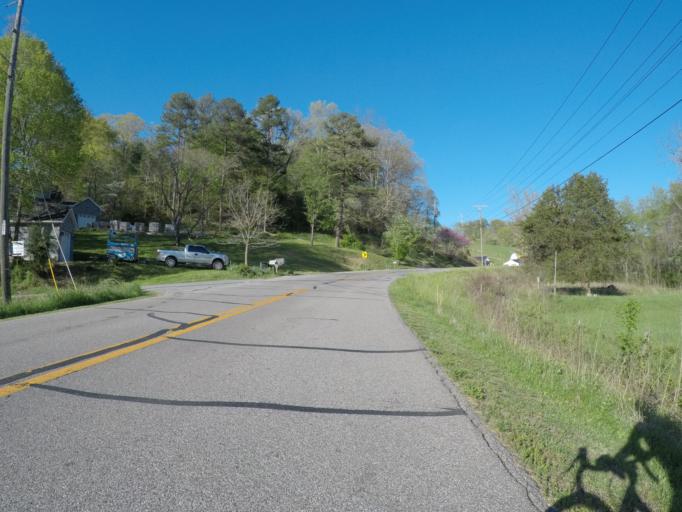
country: US
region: Kentucky
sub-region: Boyd County
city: Meads
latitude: 38.3705
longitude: -82.6605
